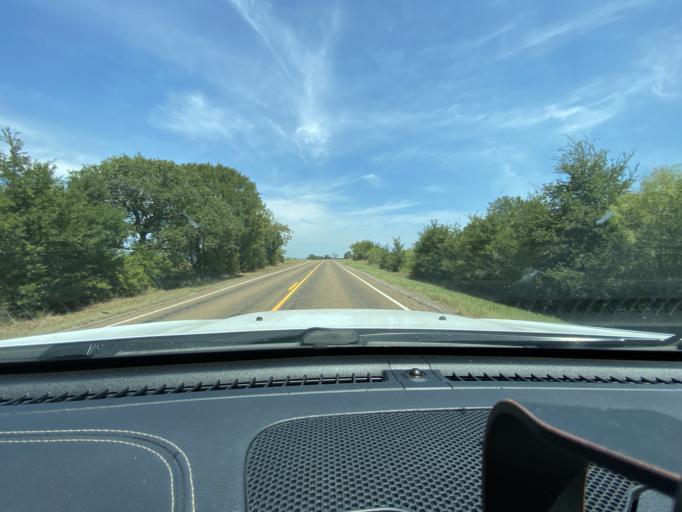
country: US
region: Texas
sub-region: Bastrop County
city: Smithville
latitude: 30.1124
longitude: -97.0806
